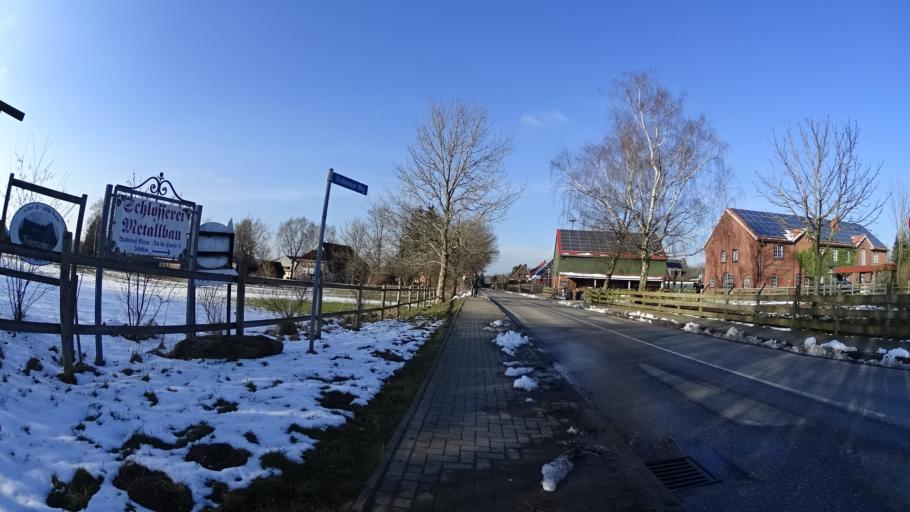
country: DE
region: Schleswig-Holstein
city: Martensrade
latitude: 54.2908
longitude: 10.3832
